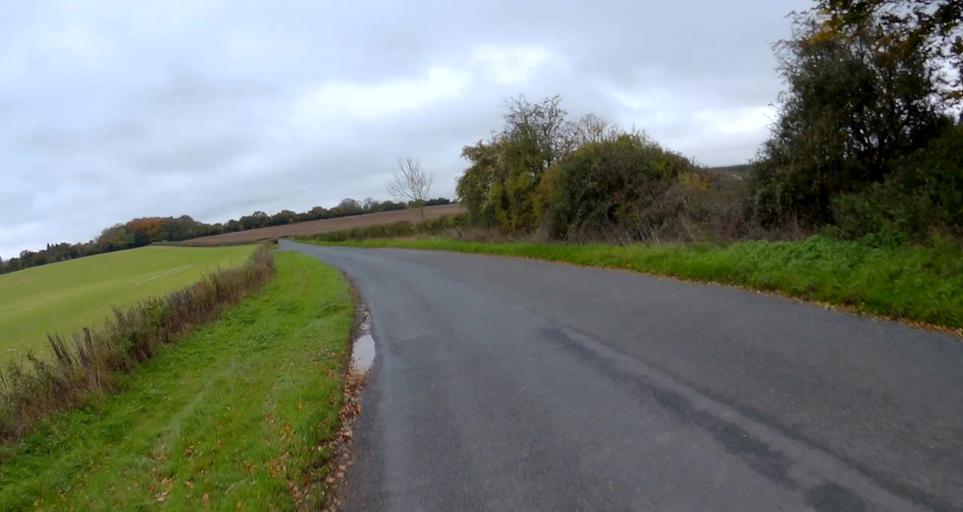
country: GB
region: England
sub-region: Hampshire
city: Basingstoke
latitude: 51.2263
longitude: -1.1267
